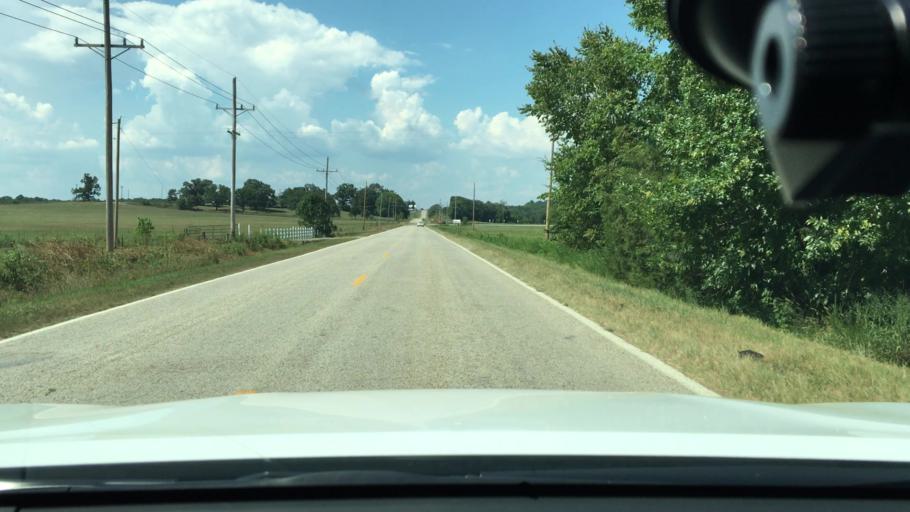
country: US
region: Arkansas
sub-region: Logan County
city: Paris
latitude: 35.3329
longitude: -93.6319
